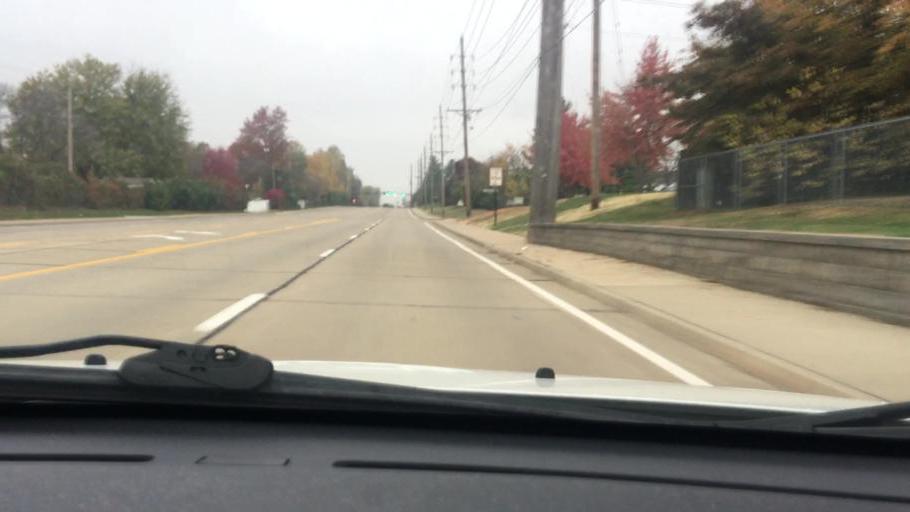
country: US
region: Missouri
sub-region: Saint Charles County
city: O'Fallon
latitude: 38.8218
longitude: -90.6864
